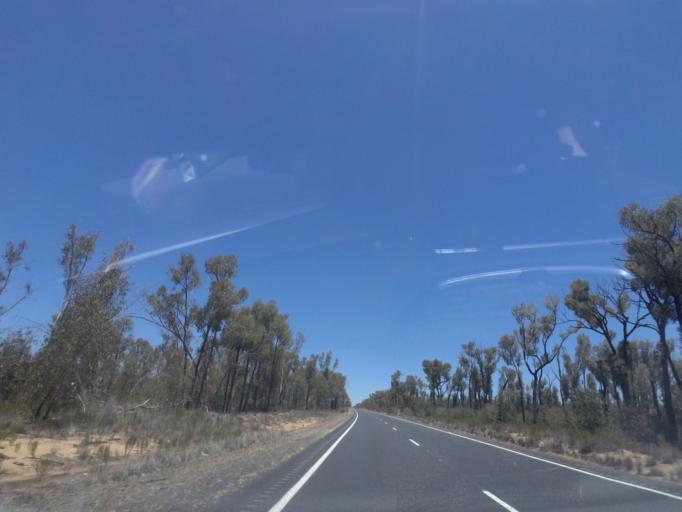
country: AU
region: New South Wales
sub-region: Warrumbungle Shire
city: Coonabarabran
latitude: -30.9460
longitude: 149.4222
